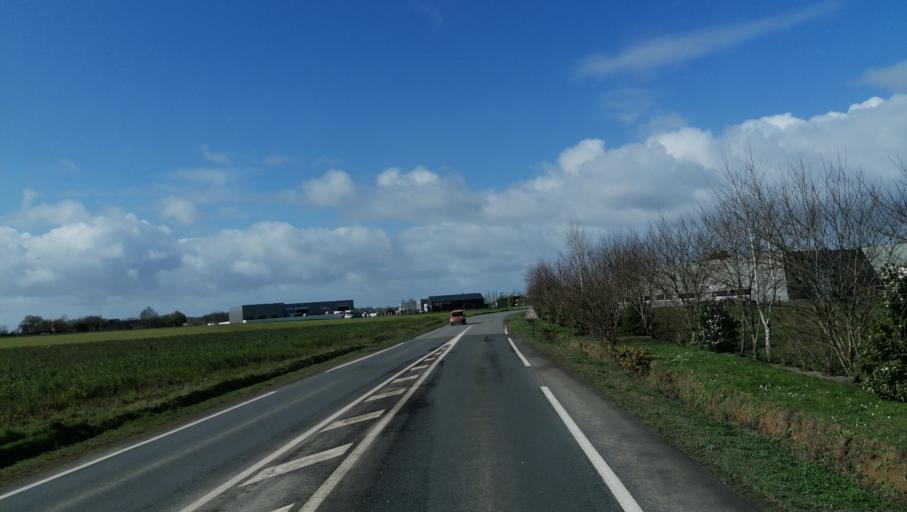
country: FR
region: Brittany
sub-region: Departement des Cotes-d'Armor
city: Tremuson
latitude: 48.5287
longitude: -2.8531
